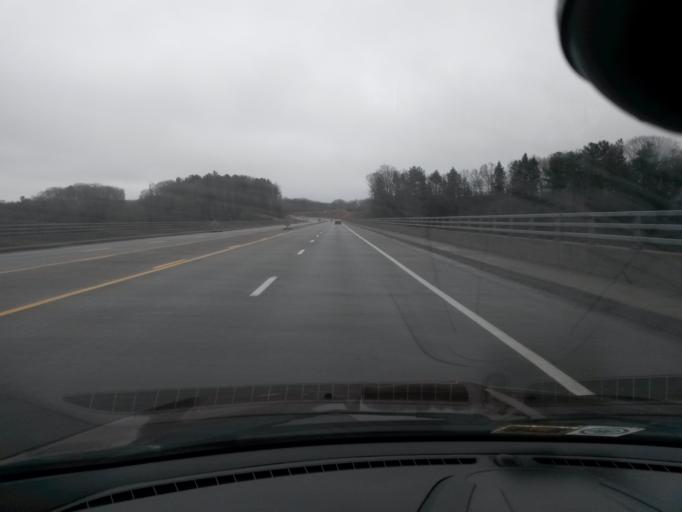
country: US
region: West Virginia
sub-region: Raleigh County
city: Beckley
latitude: 37.7922
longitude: -81.1653
